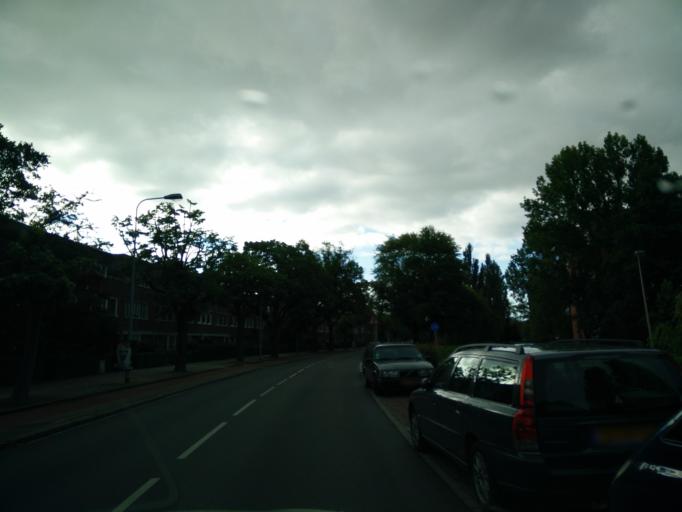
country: NL
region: Groningen
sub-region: Gemeente Groningen
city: Groningen
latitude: 53.2249
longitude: 6.5749
